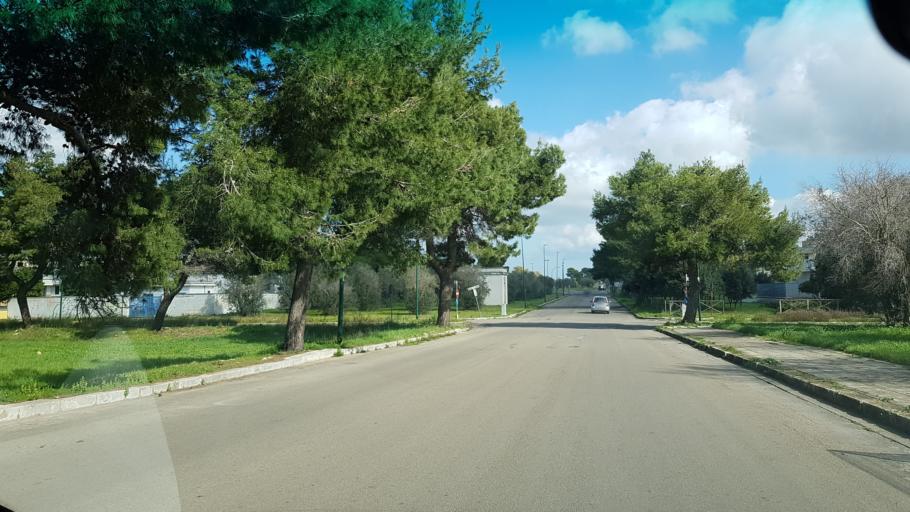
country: IT
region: Apulia
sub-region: Provincia di Lecce
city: Campi Salentina
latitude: 40.3950
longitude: 18.0294
